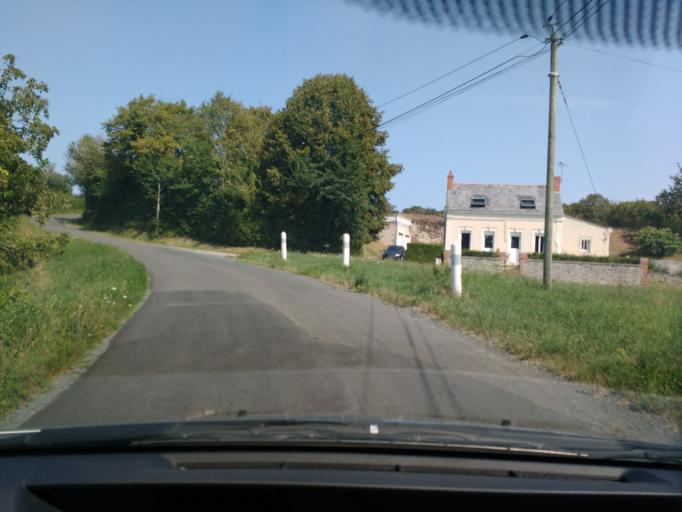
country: FR
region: Pays de la Loire
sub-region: Departement de Maine-et-Loire
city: Bauge-en-Anjou
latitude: 47.5420
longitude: -0.0374
